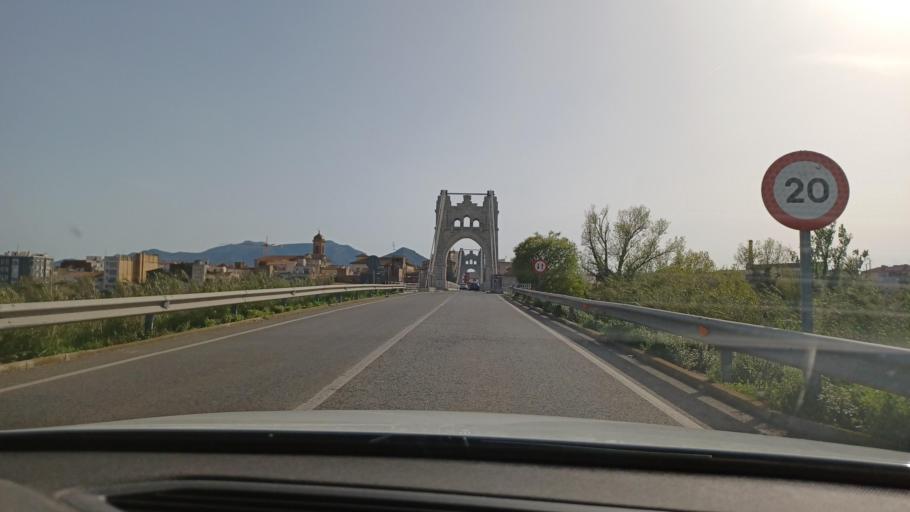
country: ES
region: Catalonia
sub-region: Provincia de Tarragona
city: Amposta
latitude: 40.7161
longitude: 0.5829
